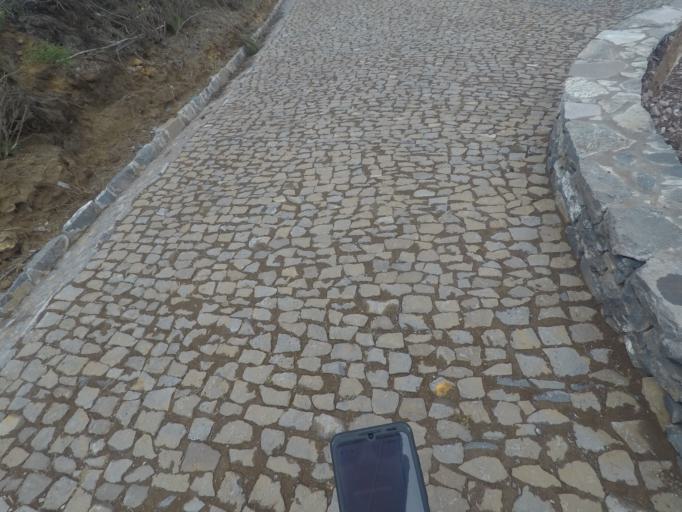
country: PT
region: Madeira
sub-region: Calheta
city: Arco da Calheta
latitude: 32.7377
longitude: -17.0989
